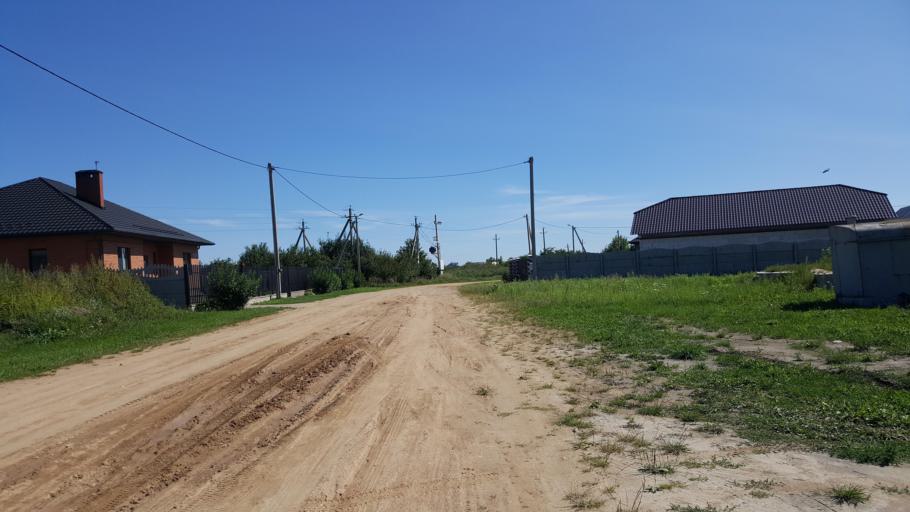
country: BY
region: Brest
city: Charnawchytsy
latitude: 52.2084
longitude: 23.7517
